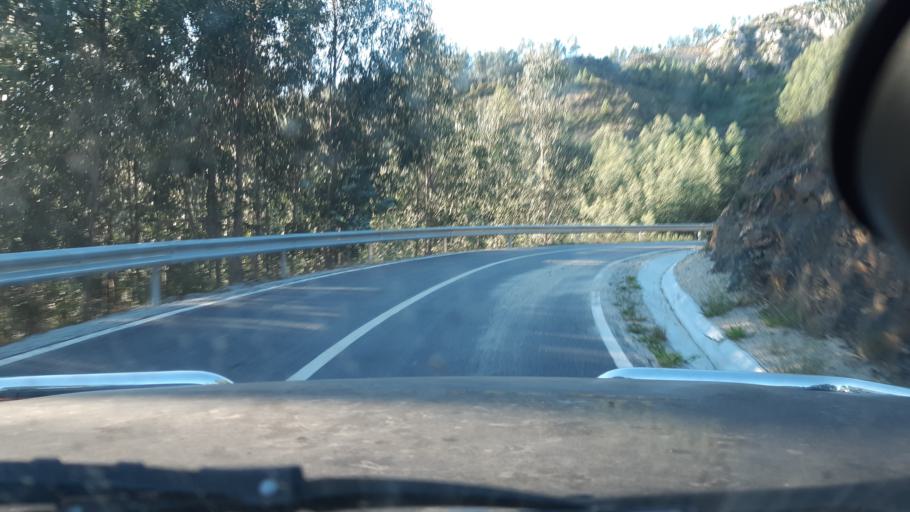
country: PT
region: Viseu
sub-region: Mortagua
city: Mortagua
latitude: 40.5388
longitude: -8.2471
